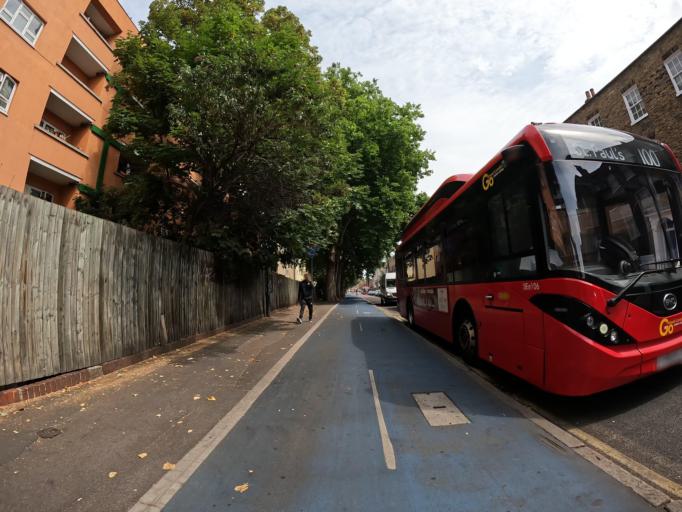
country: GB
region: England
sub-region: Greater London
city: Bethnal Green
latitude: 51.5102
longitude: -0.0610
